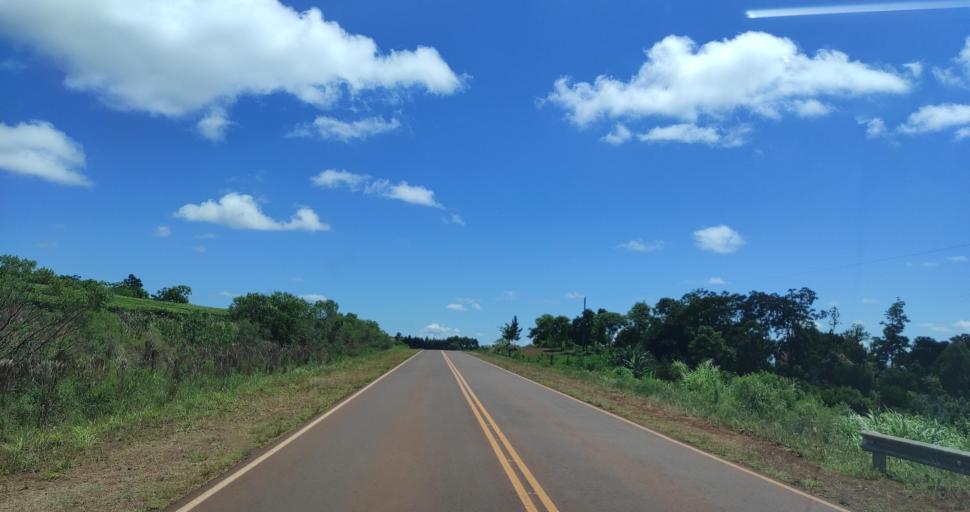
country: AR
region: Misiones
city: Campo Grande
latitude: -27.2823
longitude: -54.9089
